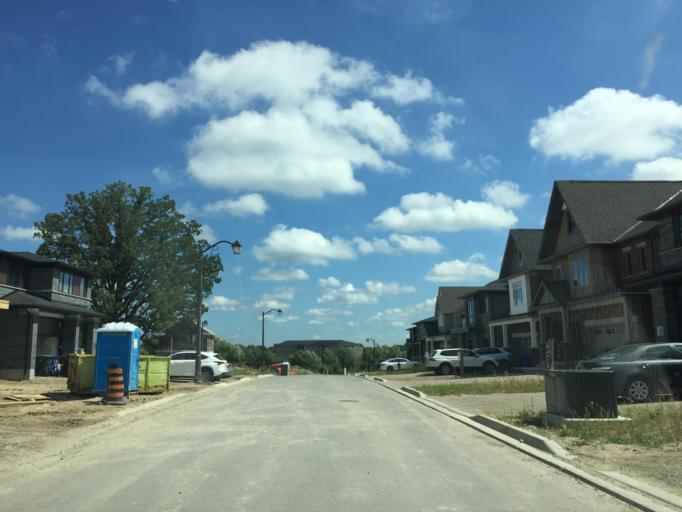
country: CA
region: Ontario
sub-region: Wellington County
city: Guelph
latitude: 43.5163
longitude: -80.2137
